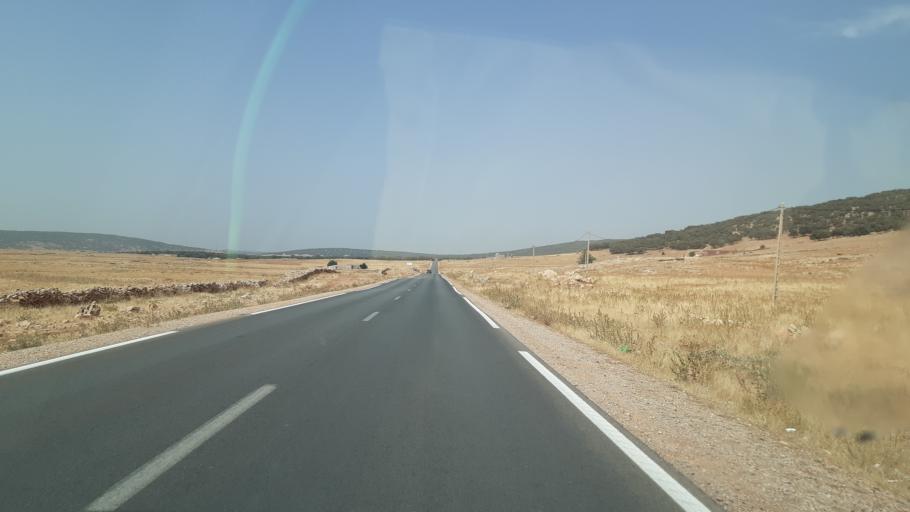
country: MA
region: Meknes-Tafilalet
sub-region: Ifrane
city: Ifrane
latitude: 33.6226
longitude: -5.0803
